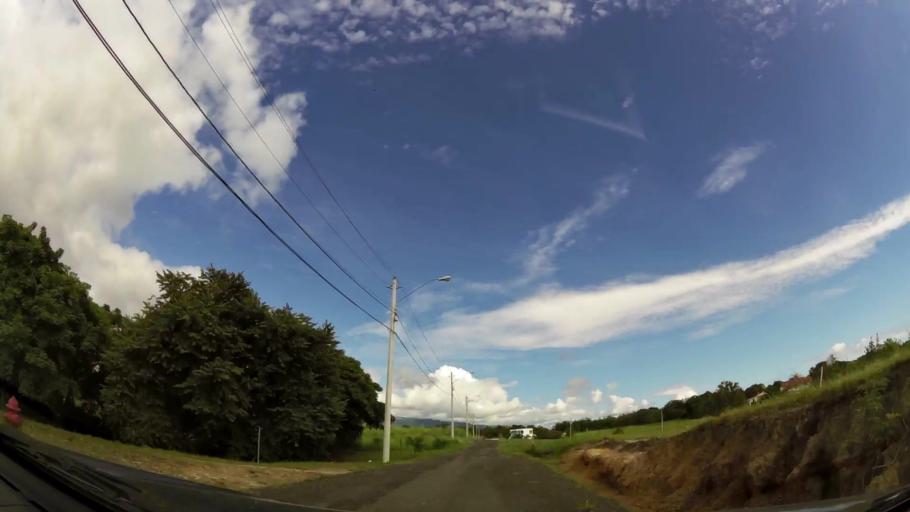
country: PA
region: Panama
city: Nueva Gorgona
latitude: 8.5388
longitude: -79.8980
